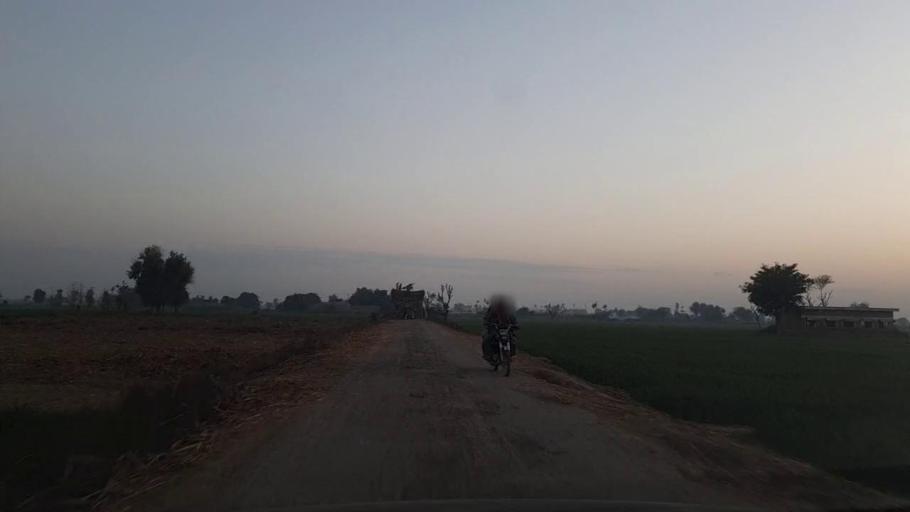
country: PK
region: Sindh
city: Daur
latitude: 26.4781
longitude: 68.4875
